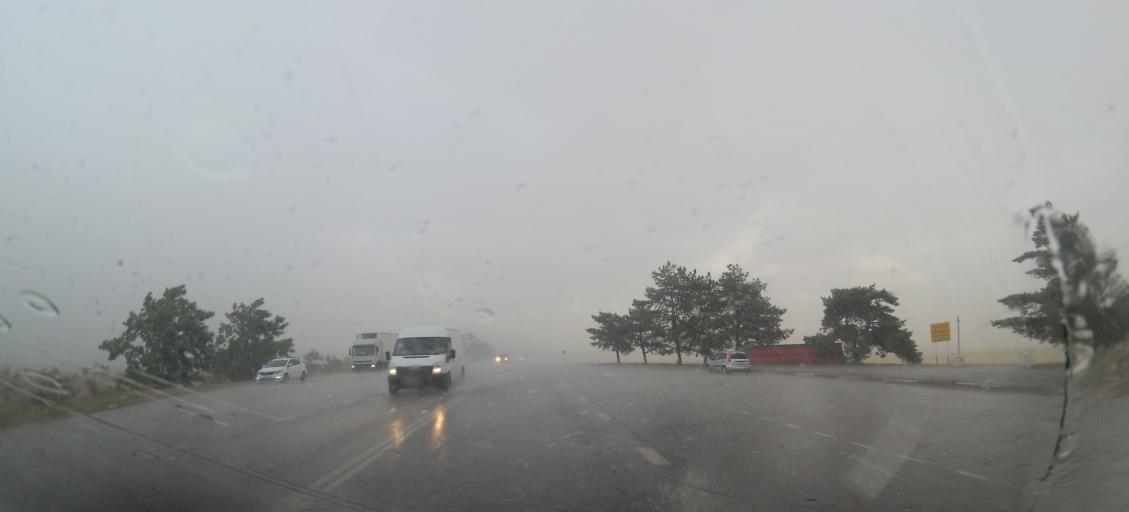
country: RU
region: Rostov
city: Proletarsk
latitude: 46.6842
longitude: 41.7214
